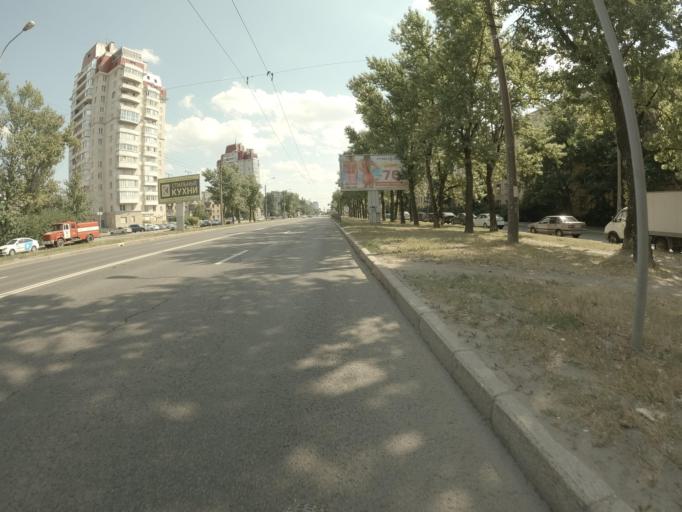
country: RU
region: St.-Petersburg
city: Avtovo
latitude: 59.8560
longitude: 30.2974
